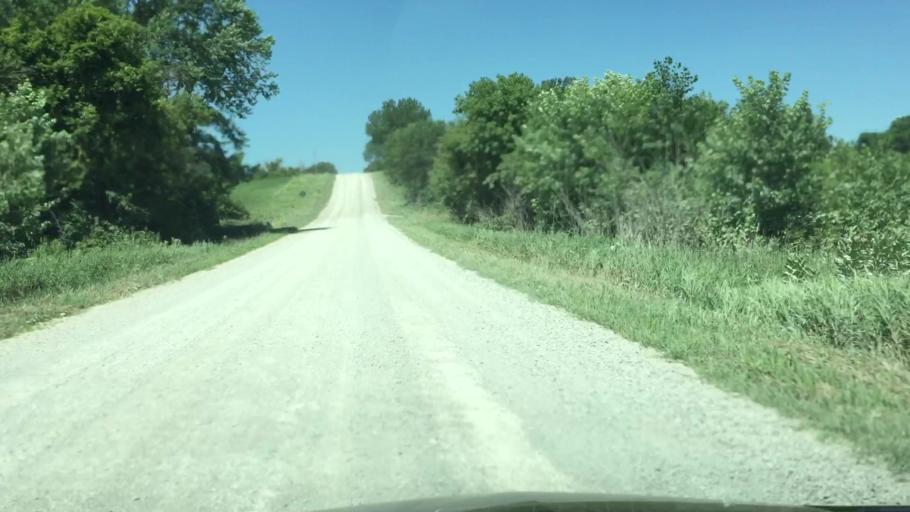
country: US
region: Iowa
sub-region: Linn County
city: Ely
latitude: 41.8325
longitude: -91.5615
